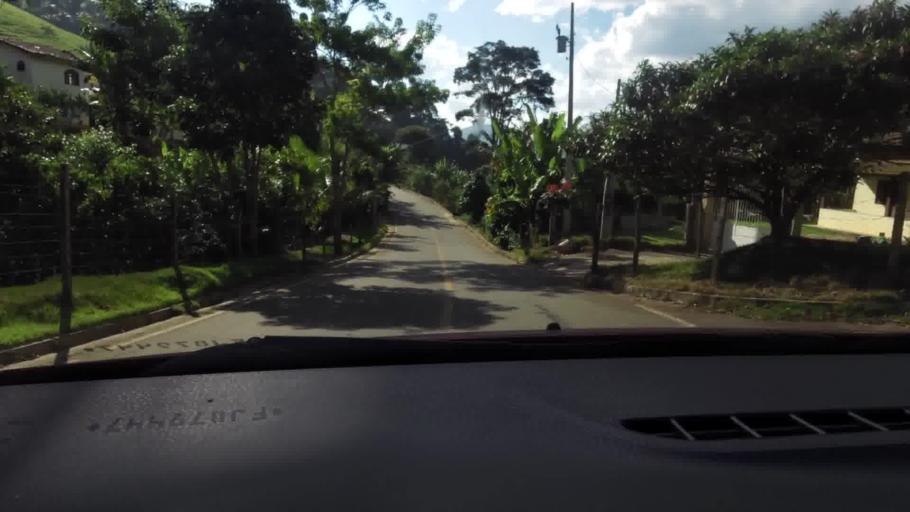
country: BR
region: Espirito Santo
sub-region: Guarapari
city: Guarapari
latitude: -20.5484
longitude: -40.5567
